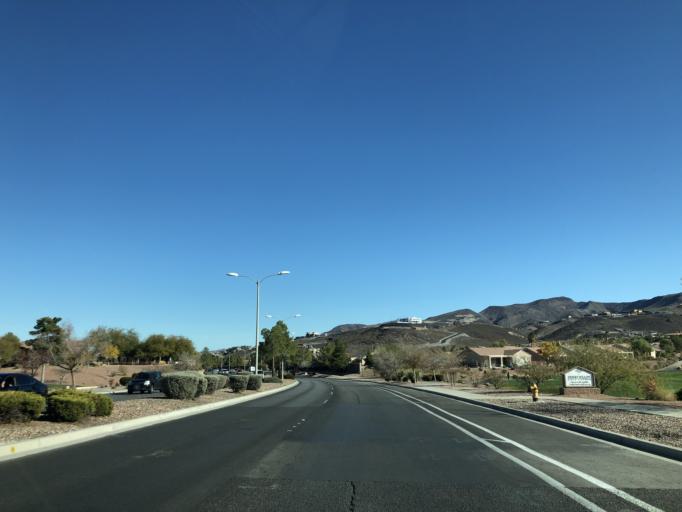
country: US
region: Nevada
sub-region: Clark County
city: Whitney
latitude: 36.0046
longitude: -115.0745
